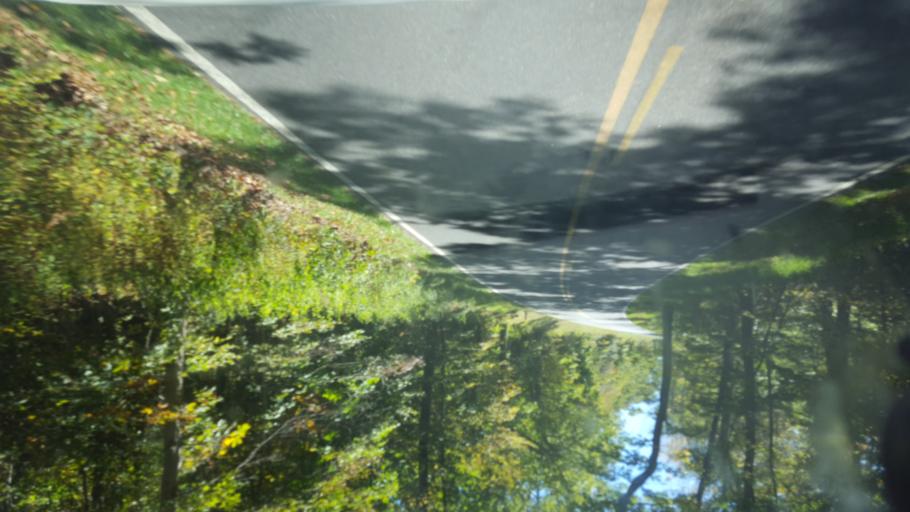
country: US
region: Virginia
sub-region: Page County
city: Stanley
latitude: 38.4457
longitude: -78.4718
